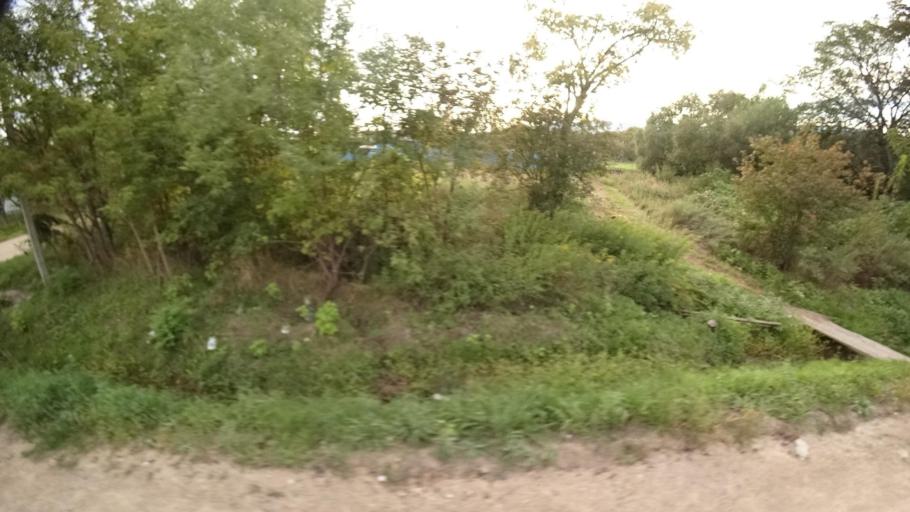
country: RU
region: Primorskiy
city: Yakovlevka
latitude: 44.4211
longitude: 133.4620
